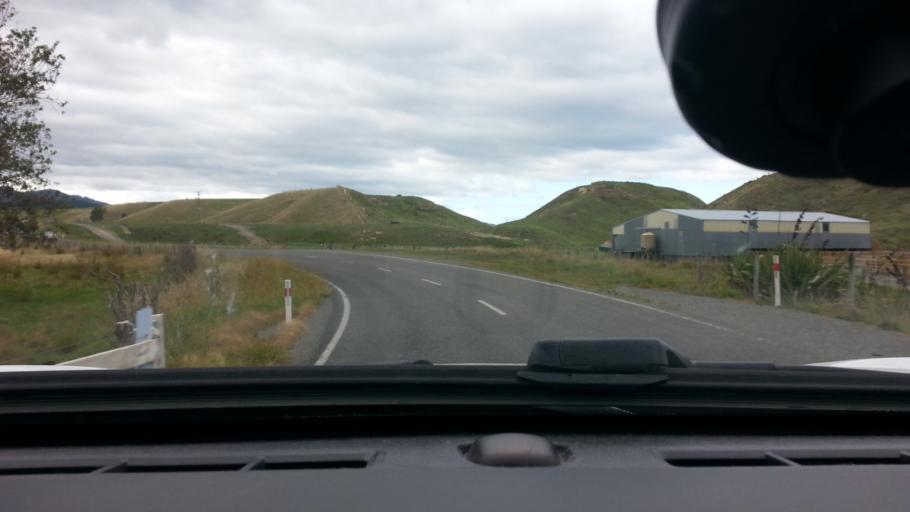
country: NZ
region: Wellington
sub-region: Upper Hutt City
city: Upper Hutt
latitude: -41.4133
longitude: 175.1965
